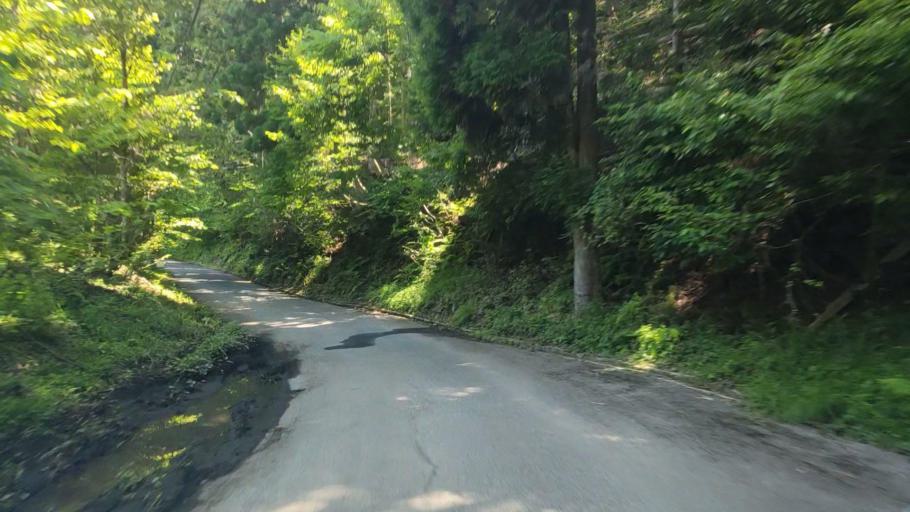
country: JP
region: Gifu
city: Godo
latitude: 35.6900
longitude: 136.5656
